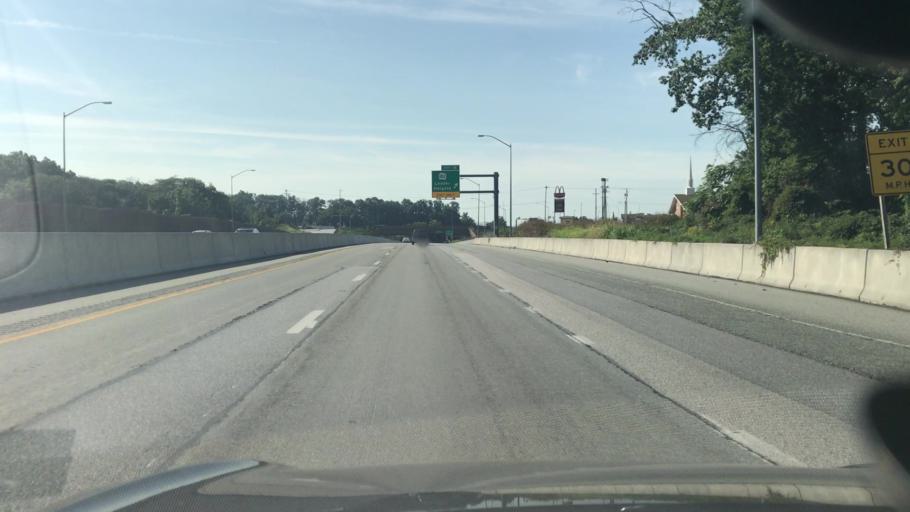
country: US
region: Pennsylvania
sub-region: York County
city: Spry
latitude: 39.9139
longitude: -76.7043
